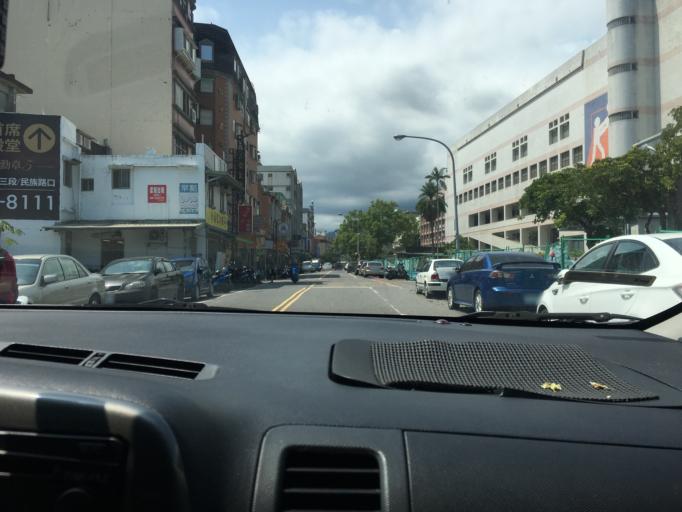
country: TW
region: Taiwan
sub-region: Yilan
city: Yilan
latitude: 24.7448
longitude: 121.7471
